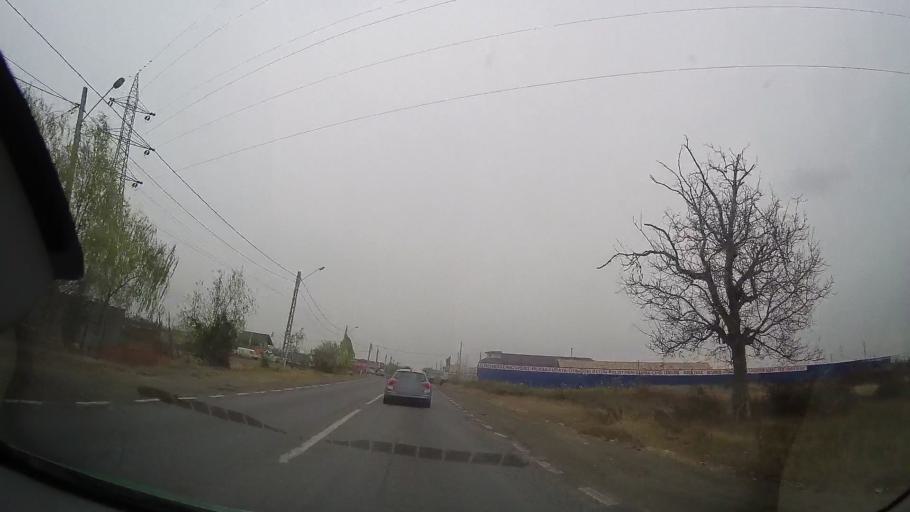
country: RO
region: Prahova
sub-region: Comuna Blejoiu
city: Ploiestiori
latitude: 44.9740
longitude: 26.0191
